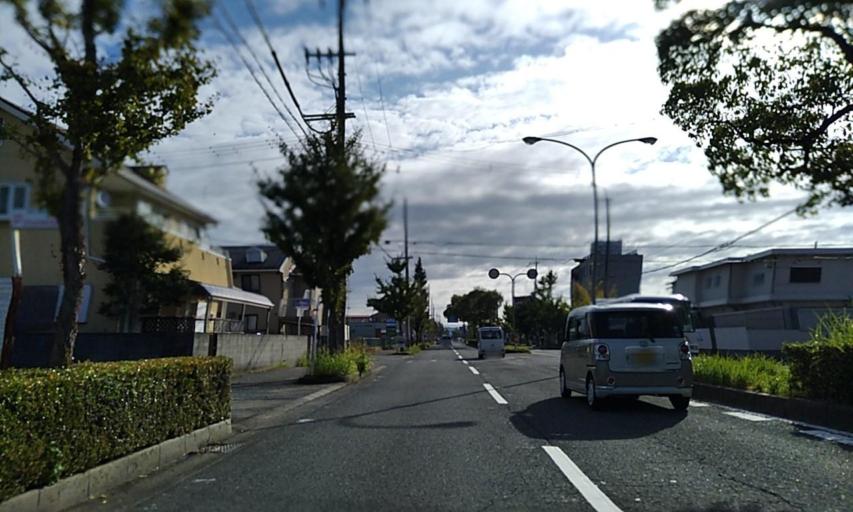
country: JP
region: Wakayama
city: Minato
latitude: 34.2572
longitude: 135.1230
